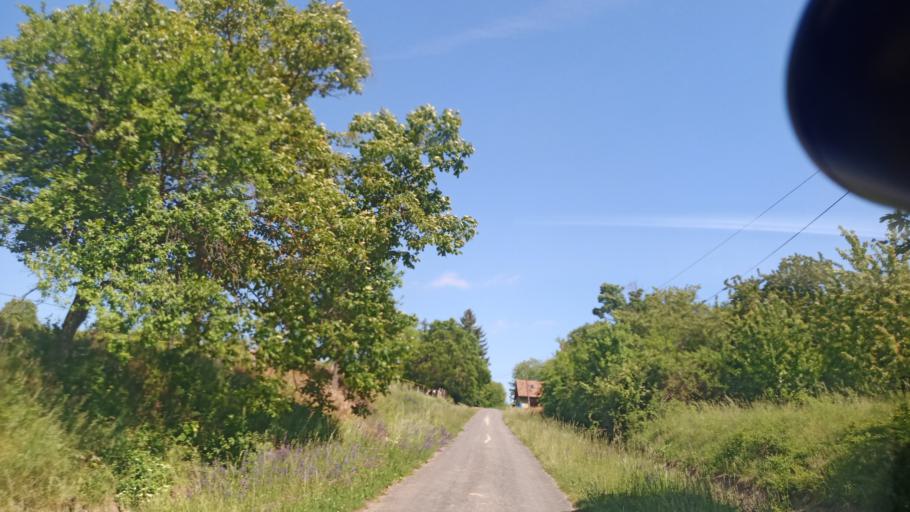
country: HU
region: Zala
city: Pacsa
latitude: 46.6541
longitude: 17.0614
